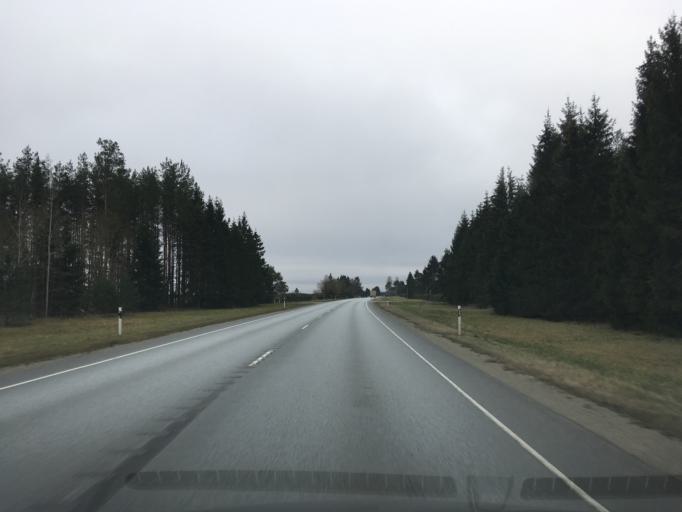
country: EE
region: Laeaene-Virumaa
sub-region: Viru-Nigula vald
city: Kunda
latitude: 59.3948
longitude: 26.6239
